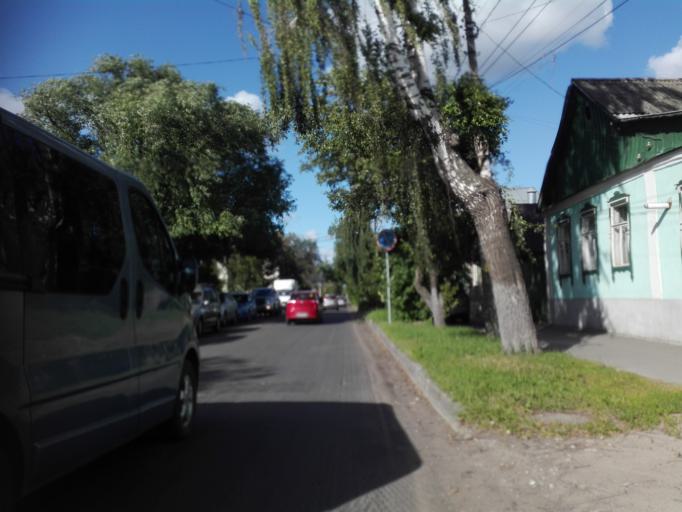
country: RU
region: Orjol
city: Orel
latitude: 52.9538
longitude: 36.0477
